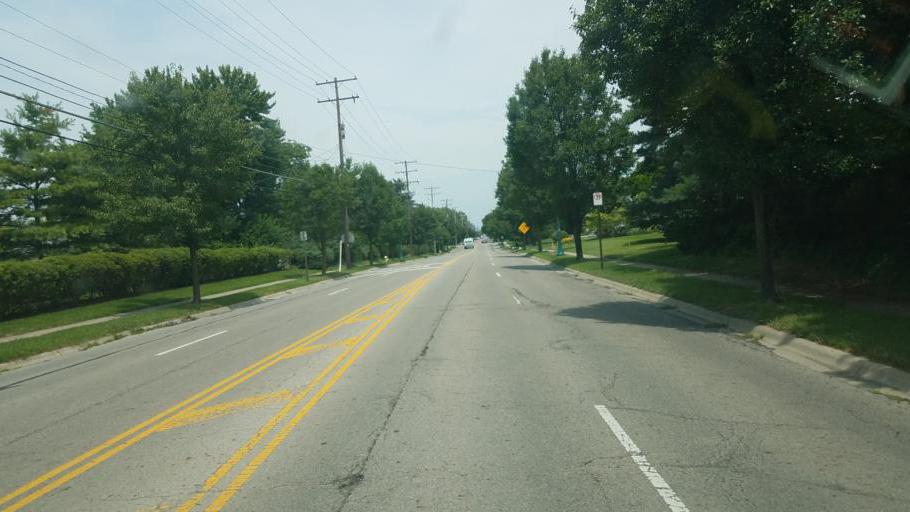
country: US
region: Ohio
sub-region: Franklin County
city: Upper Arlington
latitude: 40.0414
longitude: -83.0667
